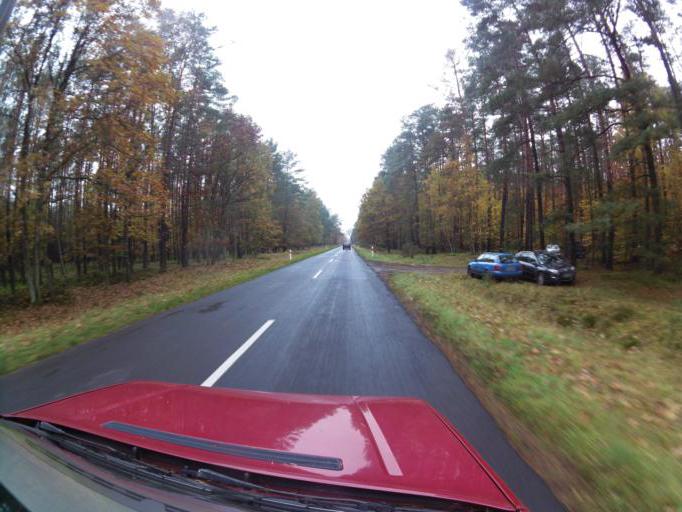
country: PL
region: West Pomeranian Voivodeship
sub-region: Powiat policki
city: Dobra
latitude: 53.5668
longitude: 14.4405
